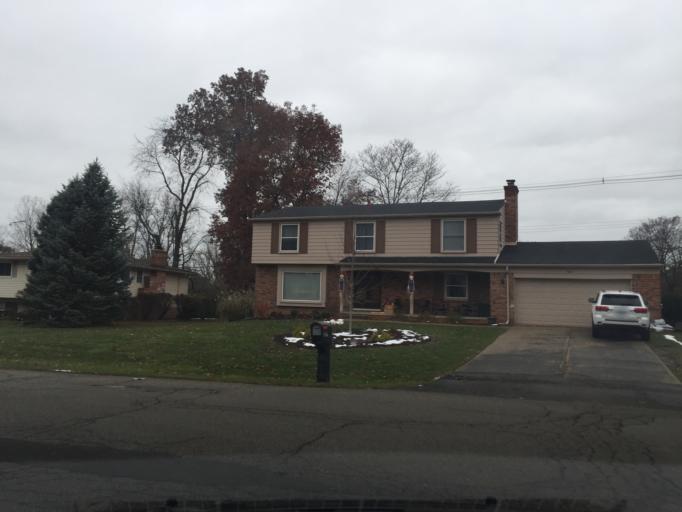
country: US
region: Michigan
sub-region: Oakland County
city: Franklin
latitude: 42.5339
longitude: -83.2910
